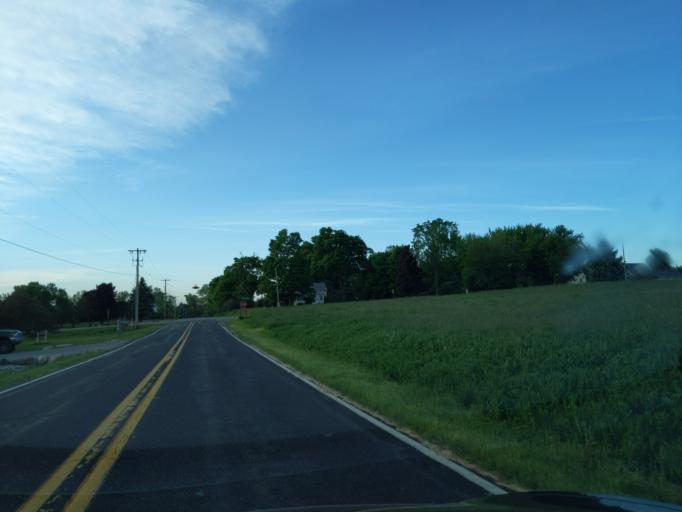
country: US
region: Michigan
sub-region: Ingham County
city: Stockbridge
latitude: 42.5334
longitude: -84.3026
